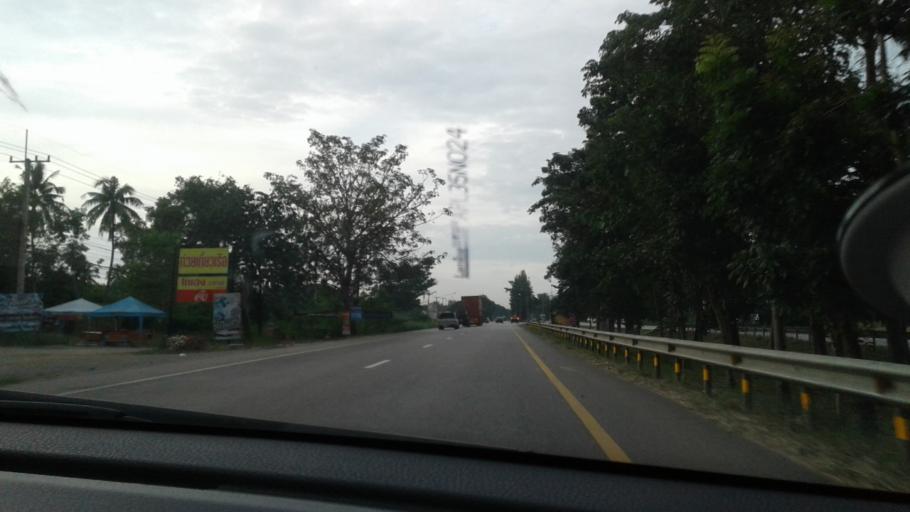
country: TH
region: Prachuap Khiri Khan
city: Pran Buri
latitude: 12.4260
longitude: 99.9195
